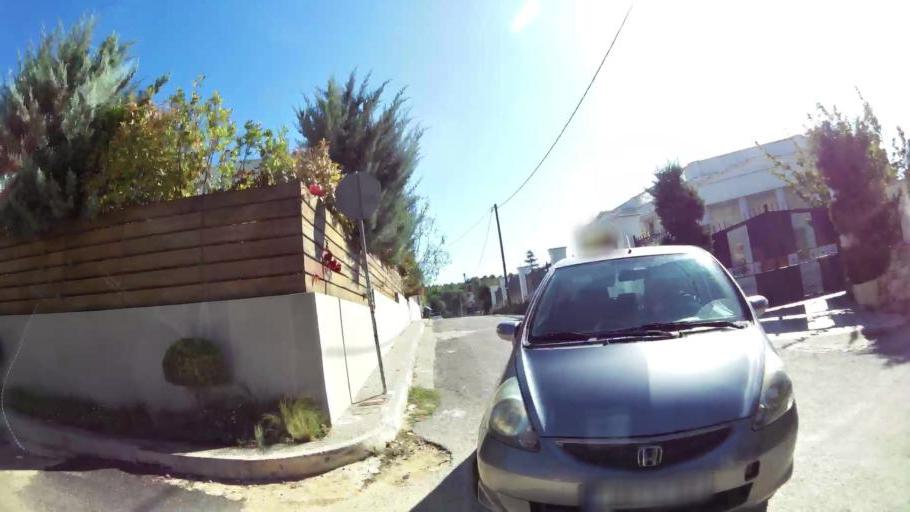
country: GR
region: Attica
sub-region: Nomarchia Anatolikis Attikis
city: Anoixi
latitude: 38.1295
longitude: 23.8595
